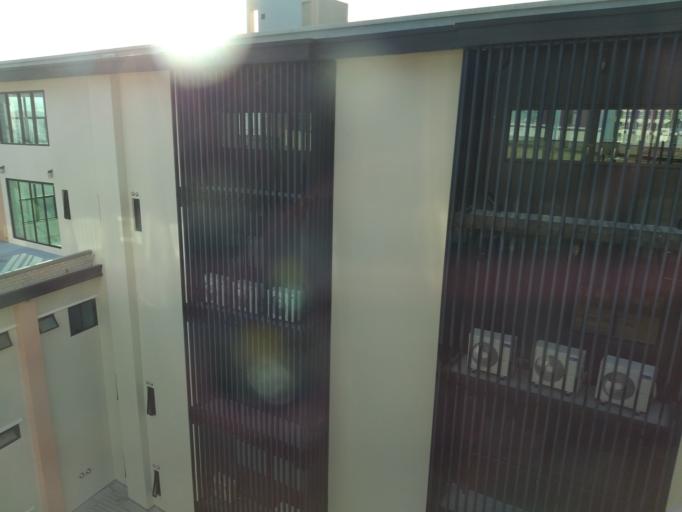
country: TH
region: Nonthaburi
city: Mueang Nonthaburi
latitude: 13.8552
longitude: 100.5188
